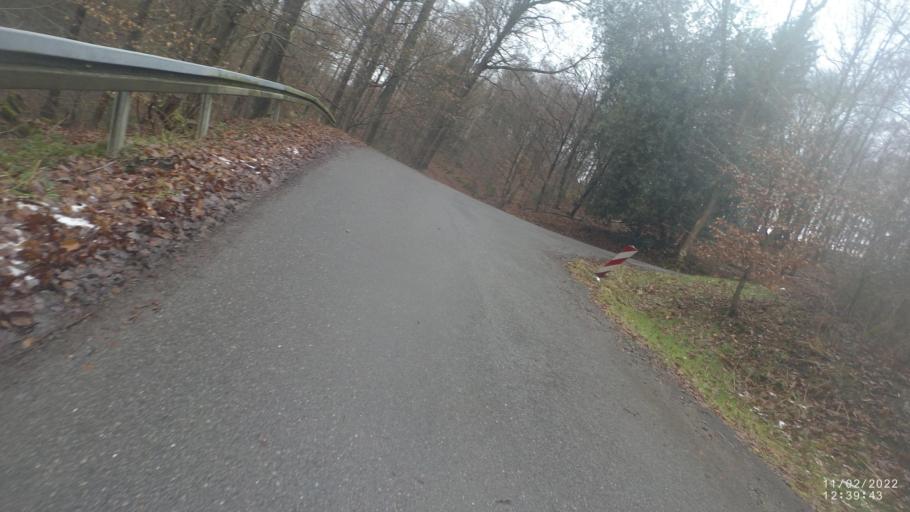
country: DE
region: North Rhine-Westphalia
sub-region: Regierungsbezirk Arnsberg
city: Nachrodt-Wiblingwerde
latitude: 51.3127
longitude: 7.6240
